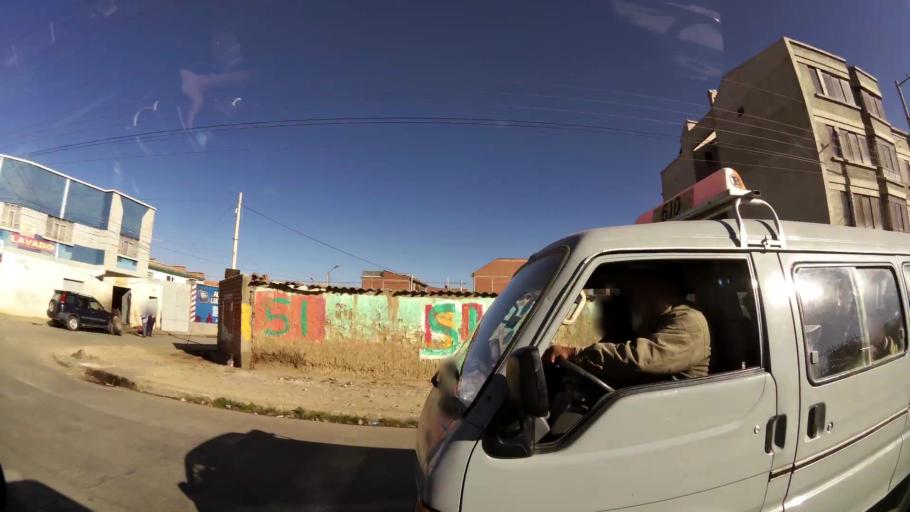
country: BO
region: La Paz
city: La Paz
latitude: -16.5249
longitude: -68.1592
